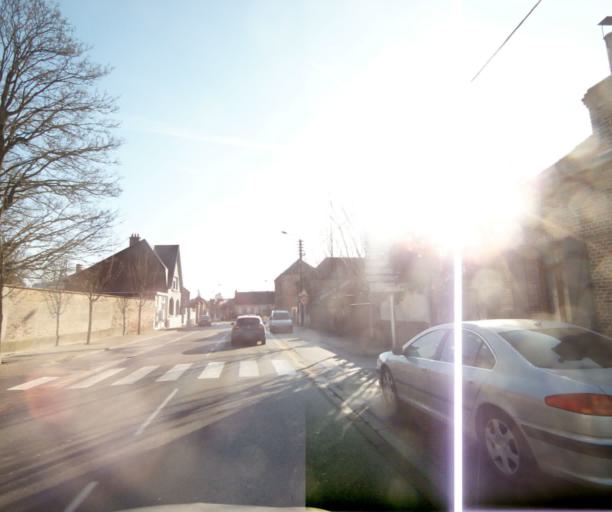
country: FR
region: Nord-Pas-de-Calais
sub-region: Departement du Nord
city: Preseau
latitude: 50.3128
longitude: 3.5758
